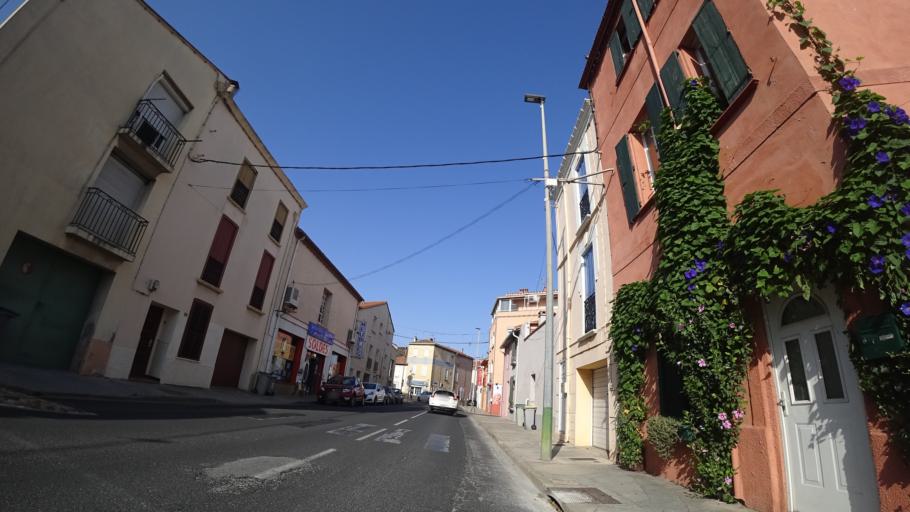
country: FR
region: Languedoc-Roussillon
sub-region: Departement des Pyrenees-Orientales
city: Saint-Laurent-de-la-Salanque
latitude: 42.7747
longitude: 2.9892
